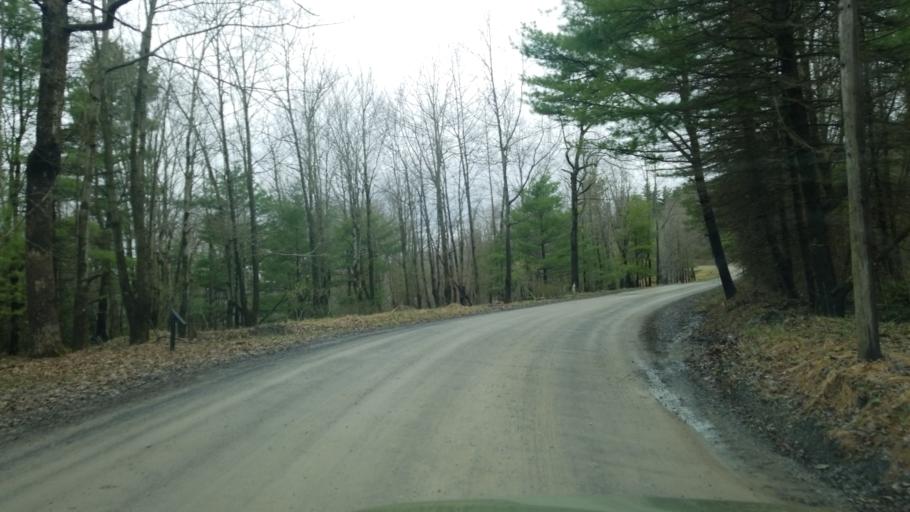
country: US
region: Pennsylvania
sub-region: Clearfield County
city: Shiloh
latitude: 41.1433
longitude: -78.3373
